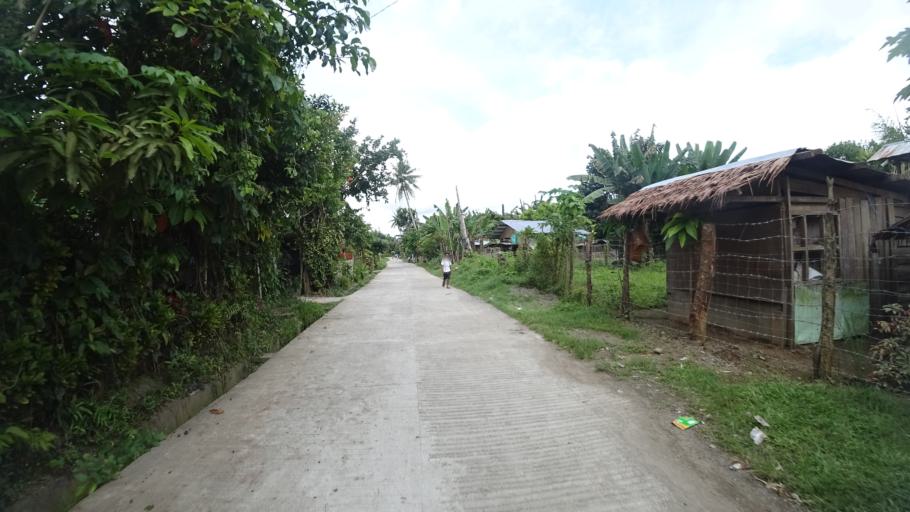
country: PH
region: Eastern Visayas
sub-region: Province of Leyte
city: Alangalang
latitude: 11.1722
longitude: 124.8635
